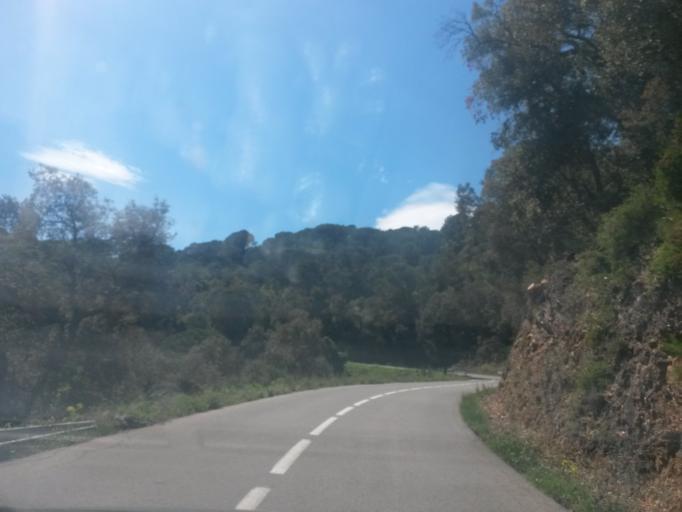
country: ES
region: Catalonia
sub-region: Provincia de Girona
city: Cassa de la Selva
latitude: 41.9243
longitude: 2.9159
